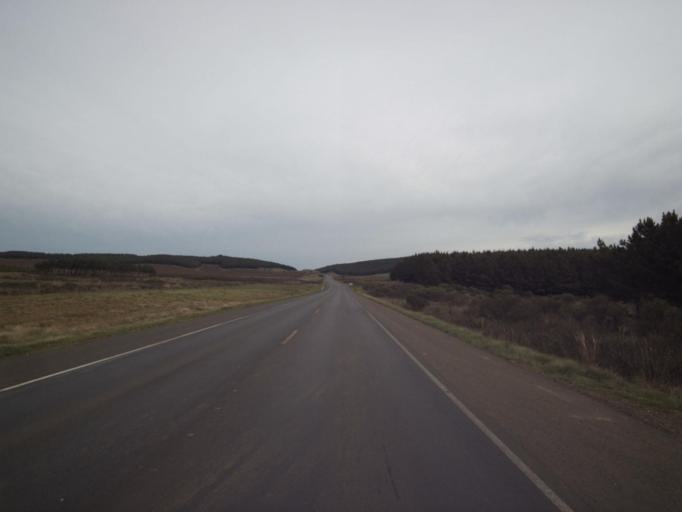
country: BR
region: Parana
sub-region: Palmas
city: Palmas
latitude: -26.6597
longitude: -51.5388
